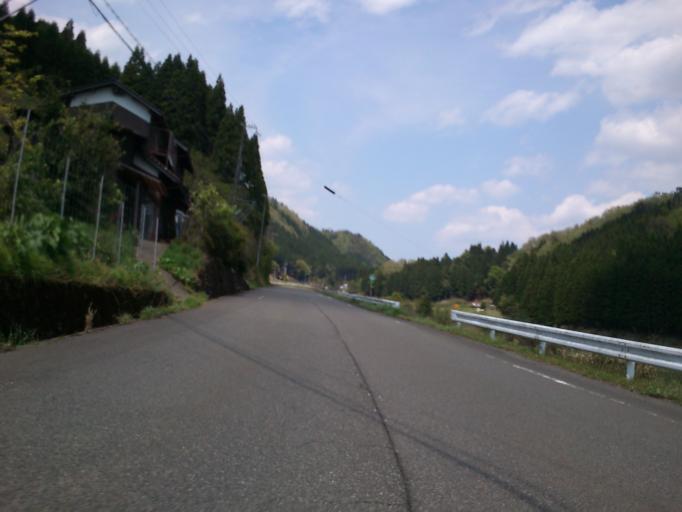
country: JP
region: Kyoto
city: Fukuchiyama
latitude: 35.3841
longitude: 134.9398
